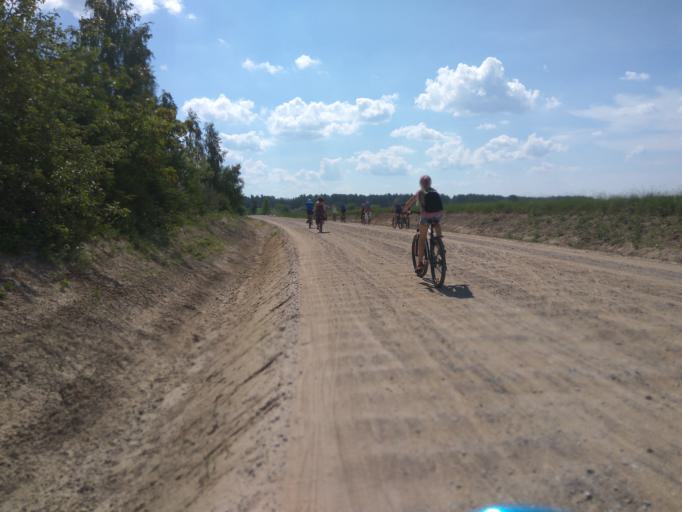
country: LV
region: Kuldigas Rajons
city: Kuldiga
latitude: 56.9493
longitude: 21.9735
